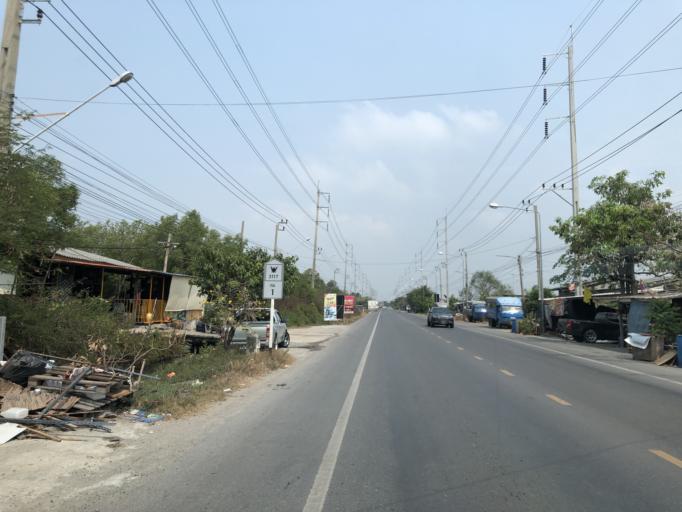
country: TH
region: Samut Prakan
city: Bang Bo
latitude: 13.5123
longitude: 100.8330
